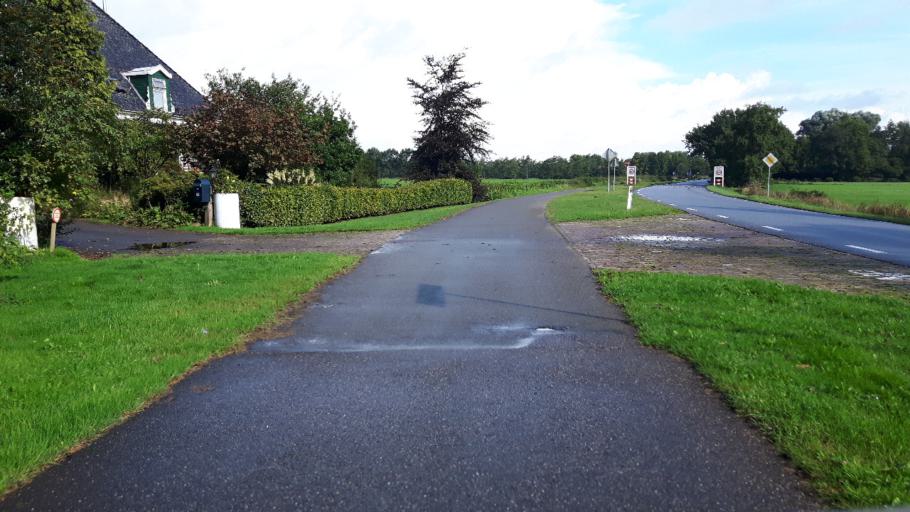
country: NL
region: Friesland
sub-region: Gemeente Smallingerland
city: Drachten
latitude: 53.0748
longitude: 6.0978
